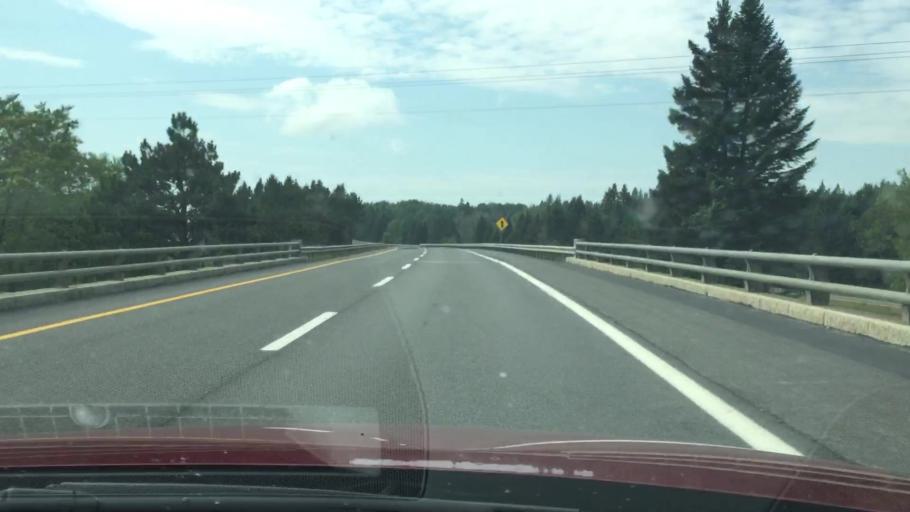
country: US
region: Maine
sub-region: Aroostook County
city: Hodgdon
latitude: 46.1106
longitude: -68.1604
